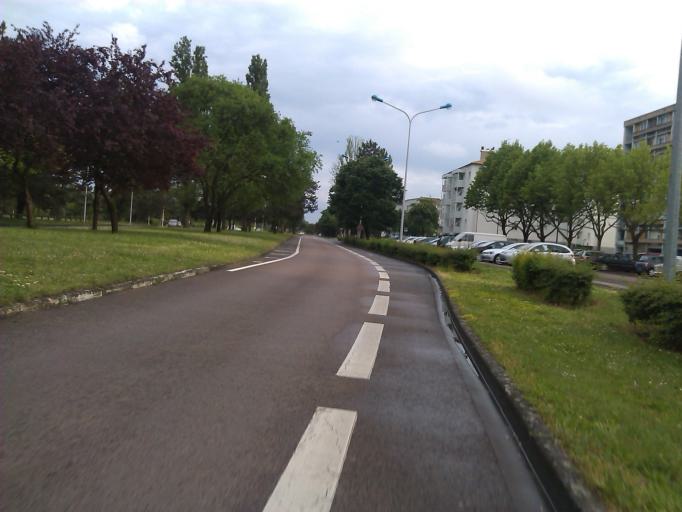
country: FR
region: Bourgogne
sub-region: Departement de Saone-et-Loire
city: Chalon-sur-Saone
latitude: 46.7935
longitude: 4.8676
